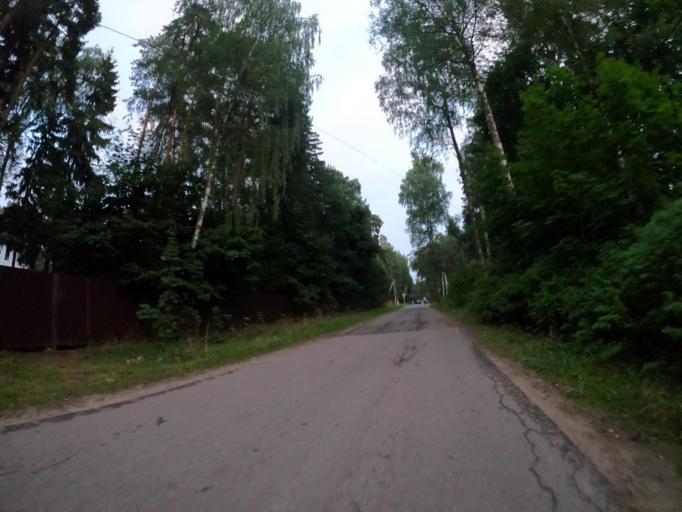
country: RU
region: Moskovskaya
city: Il'inskiy
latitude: 55.6249
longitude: 38.1047
